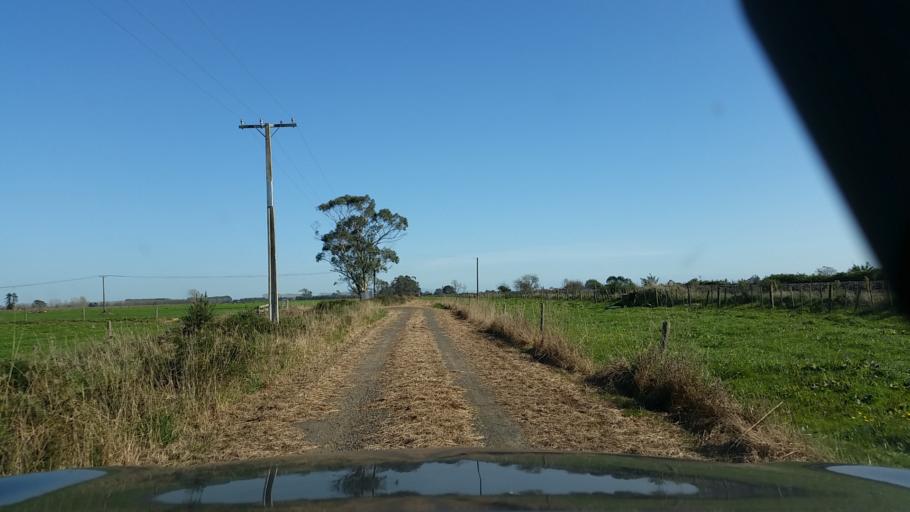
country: NZ
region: Waikato
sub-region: Waipa District
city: Cambridge
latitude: -37.6841
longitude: 175.4533
